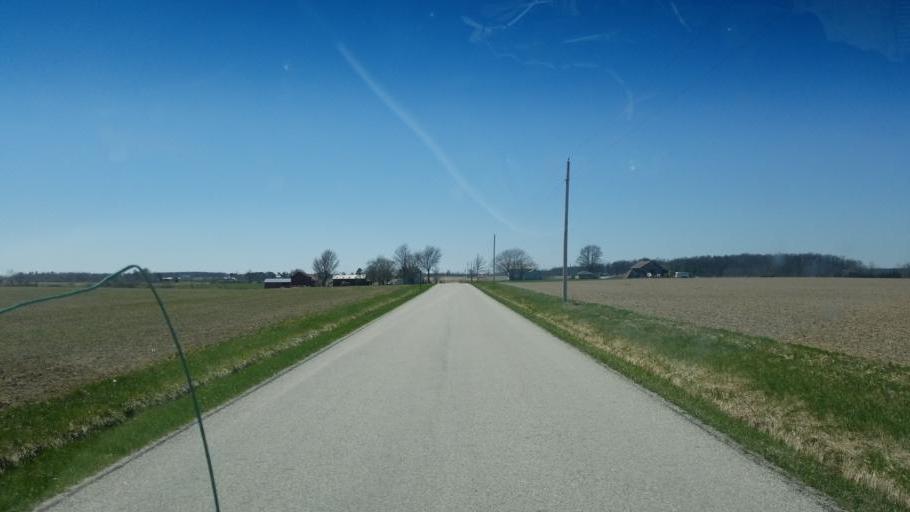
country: US
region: Ohio
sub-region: Huron County
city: Willard
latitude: 41.0837
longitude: -82.8242
